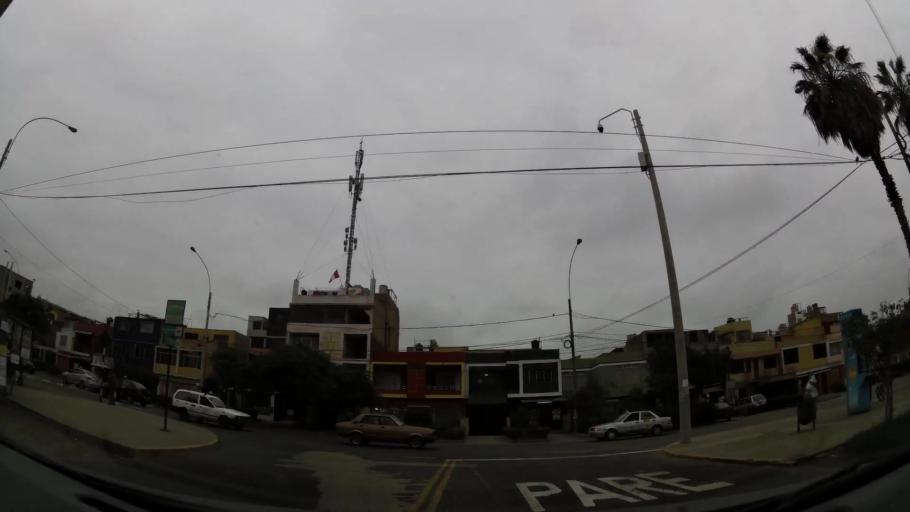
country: PE
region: Lima
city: Lima
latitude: -12.0546
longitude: -77.0708
